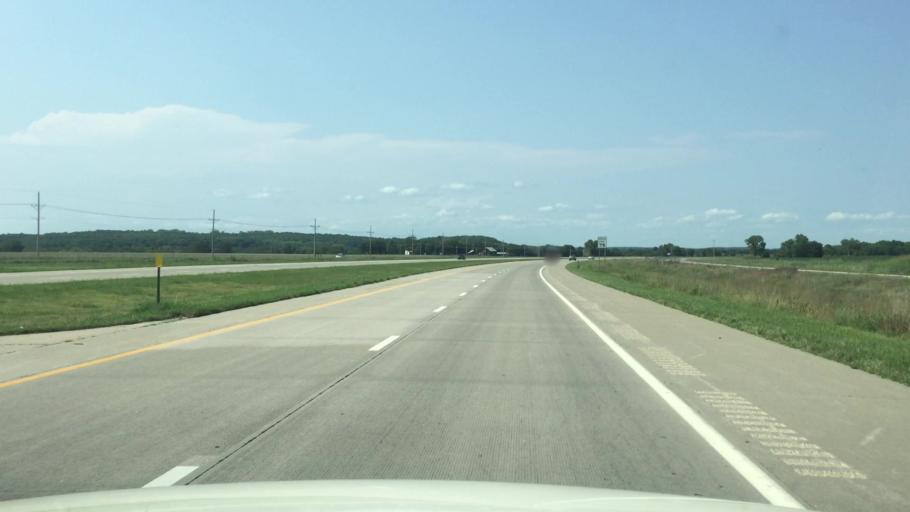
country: US
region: Kansas
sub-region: Linn County
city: Pleasanton
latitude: 38.1894
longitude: -94.7036
